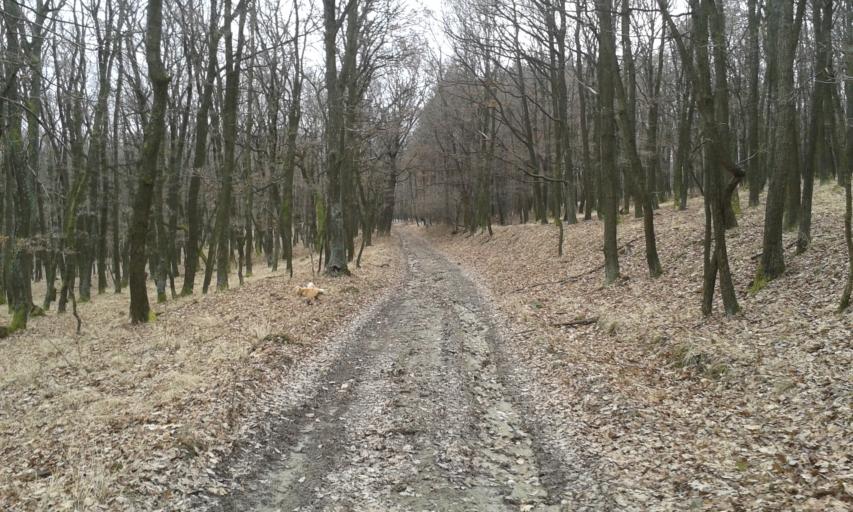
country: SK
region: Nitriansky
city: Zlate Moravce
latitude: 48.4655
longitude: 18.3038
